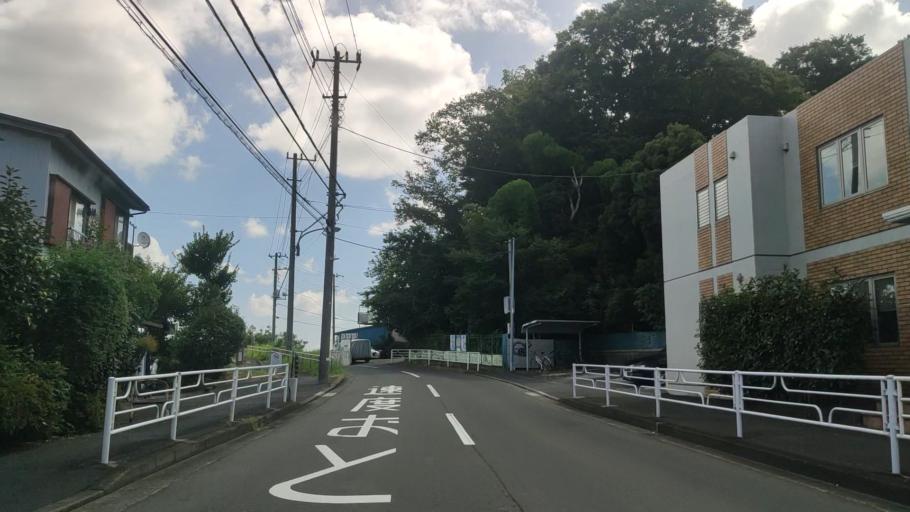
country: JP
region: Kanagawa
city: Yokohama
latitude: 35.5342
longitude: 139.6219
